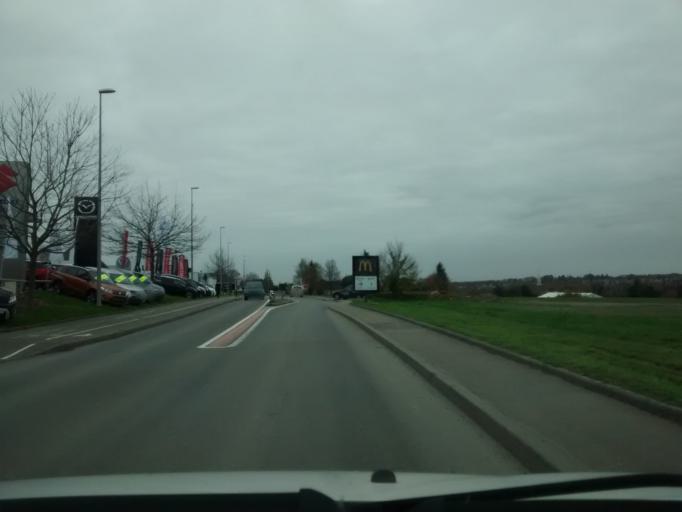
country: FR
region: Brittany
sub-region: Departement d'Ille-et-Vilaine
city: Cesson-Sevigne
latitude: 48.1158
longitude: -1.5861
